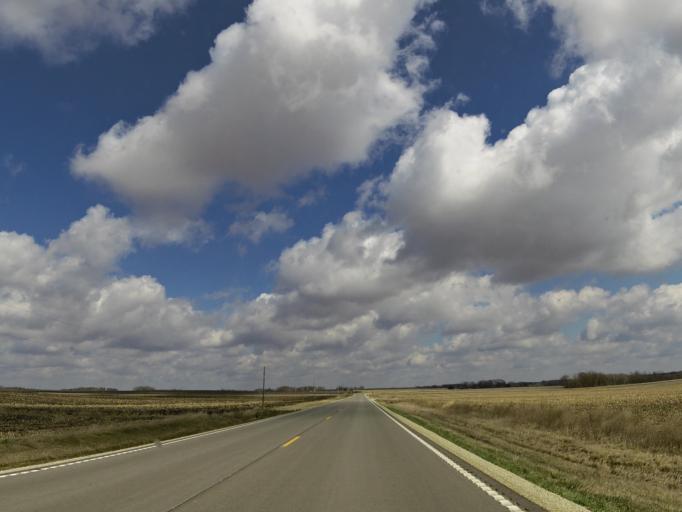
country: US
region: Minnesota
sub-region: Dodge County
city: Dodge Center
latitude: 44.0880
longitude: -92.8550
